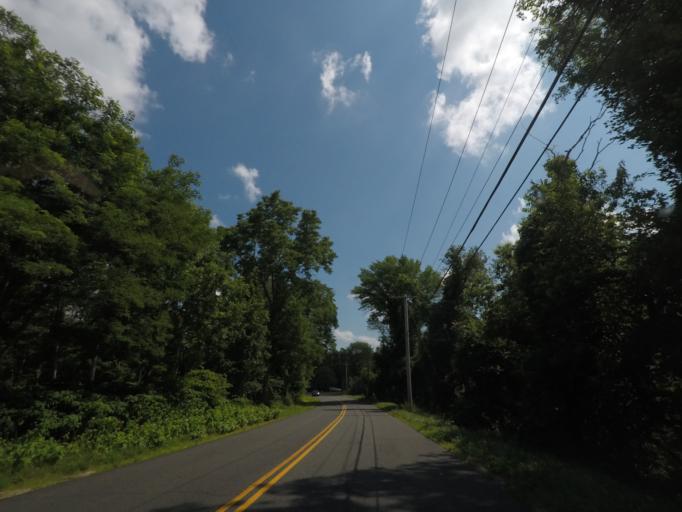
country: US
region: Massachusetts
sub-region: Hampden County
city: Monson
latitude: 42.1188
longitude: -72.3315
